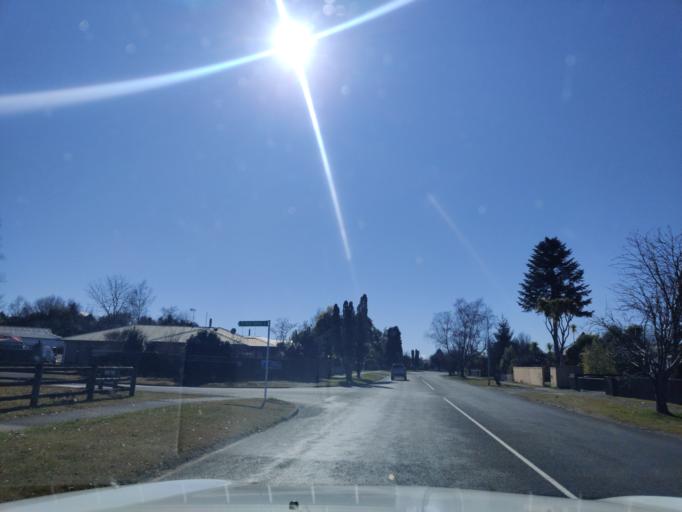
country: NZ
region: Waikato
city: Turangi
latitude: -38.9932
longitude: 175.8038
